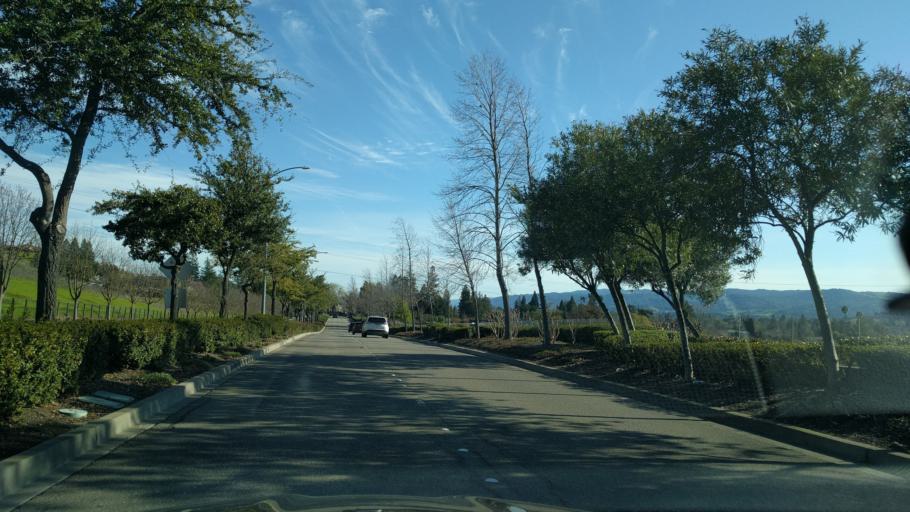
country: US
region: California
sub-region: Alameda County
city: Dublin
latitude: 37.7470
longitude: -121.9323
